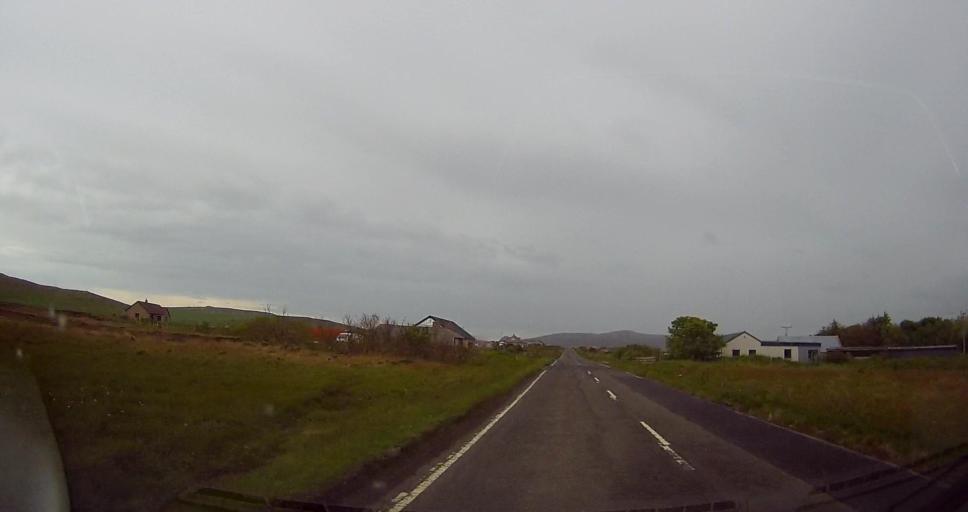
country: GB
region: Scotland
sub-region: Orkney Islands
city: Stromness
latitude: 59.0199
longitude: -3.1569
